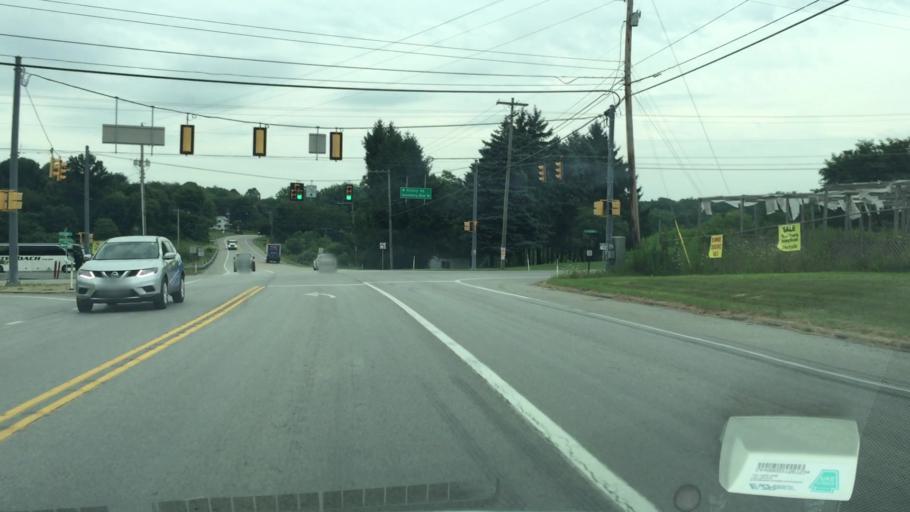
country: US
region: Pennsylvania
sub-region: Butler County
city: Saxonburg
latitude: 40.7222
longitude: -79.8534
